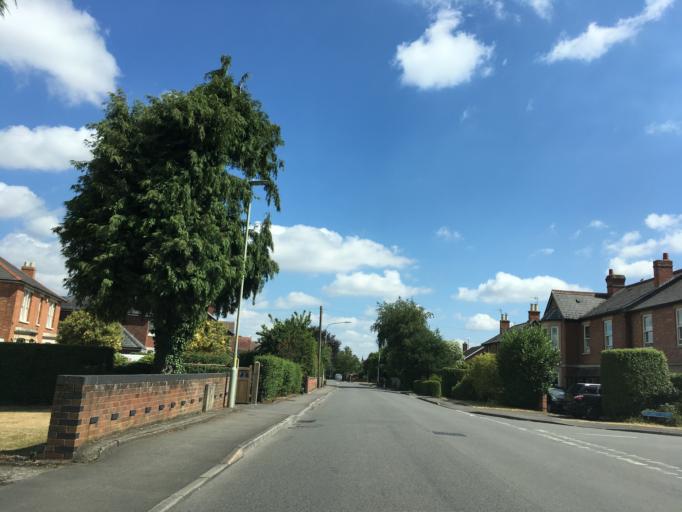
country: GB
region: England
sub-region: Gloucestershire
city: Barnwood
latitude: 51.8761
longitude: -2.2188
